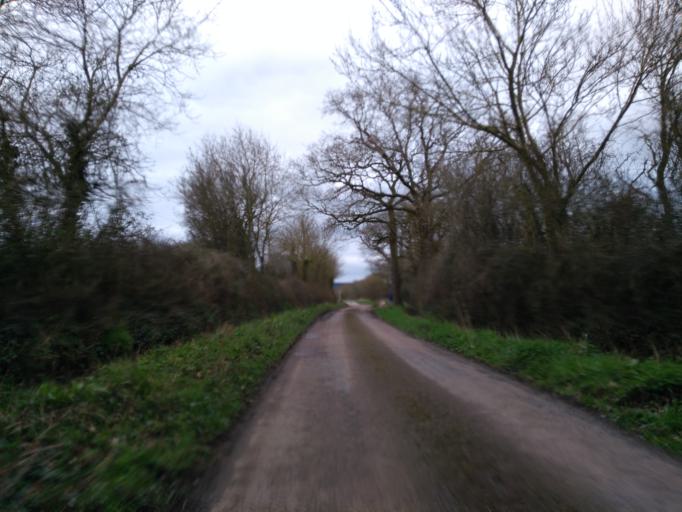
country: GB
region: England
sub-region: Devon
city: Heavitree
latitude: 50.7912
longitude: -3.5015
